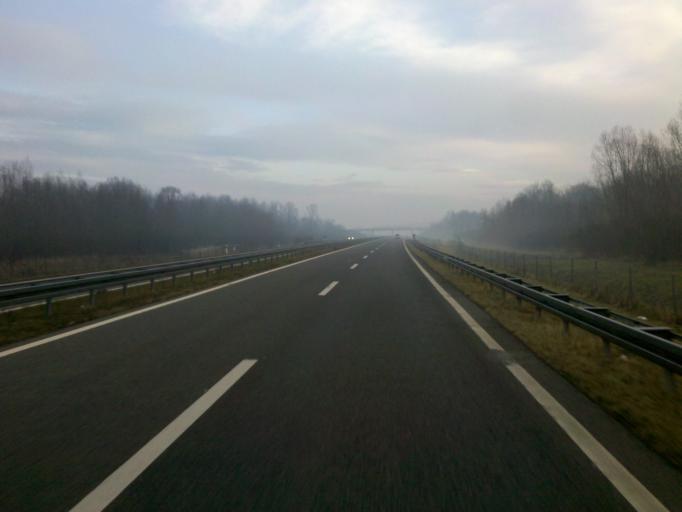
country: HR
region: Zagrebacka
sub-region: Grad Vrbovec
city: Vrbovec
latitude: 45.8813
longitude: 16.4736
